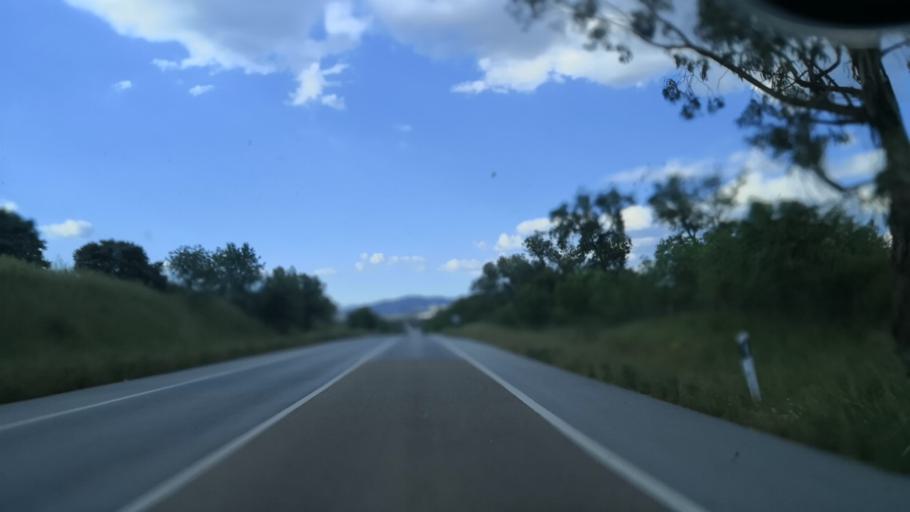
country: PT
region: Portalegre
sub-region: Portalegre
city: Urra
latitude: 39.2390
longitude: -7.4517
